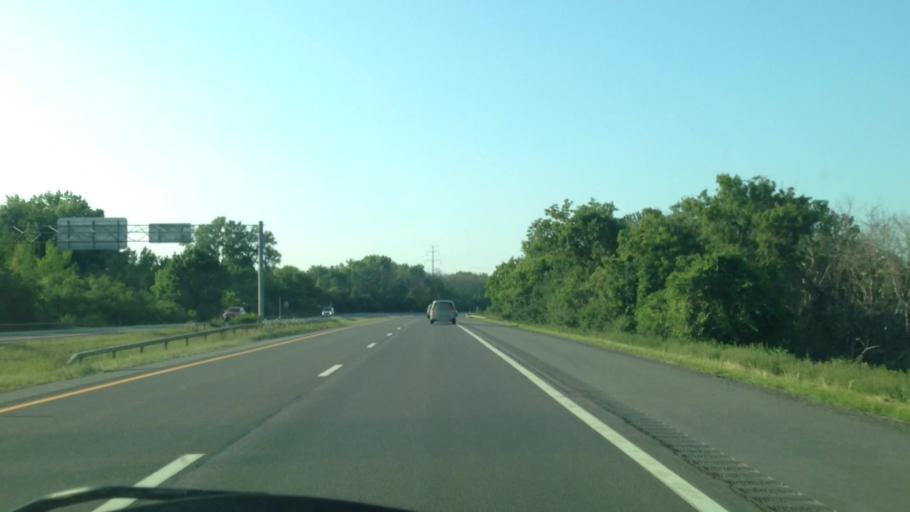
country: US
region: New York
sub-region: Onondaga County
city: East Syracuse
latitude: 43.0258
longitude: -76.0621
